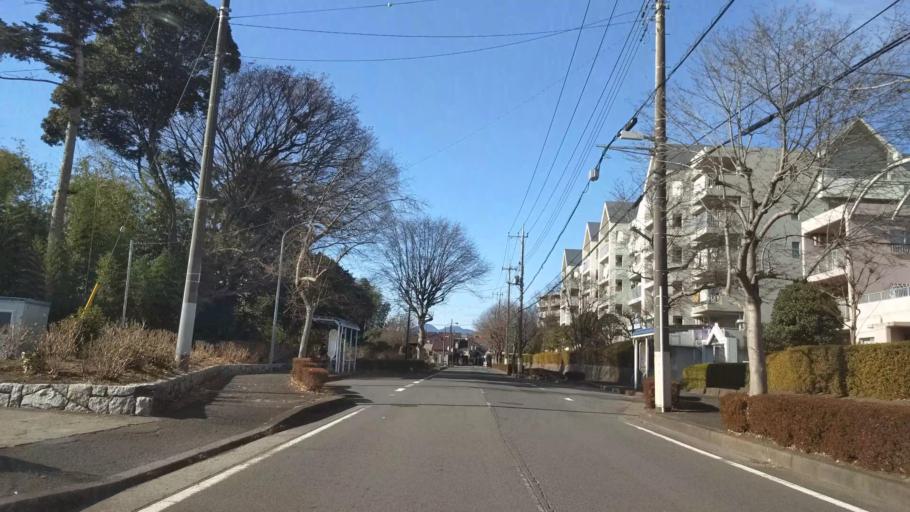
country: JP
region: Kanagawa
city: Hadano
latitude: 35.3528
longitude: 139.2265
